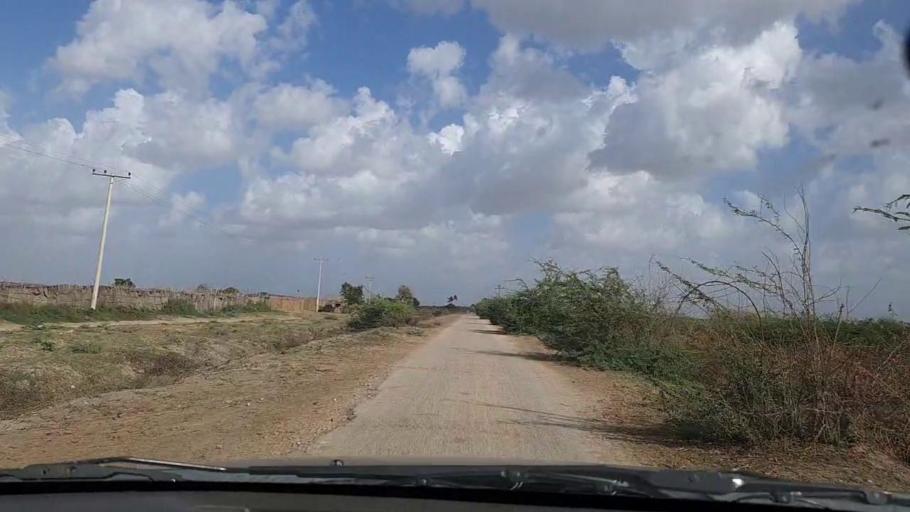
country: PK
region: Sindh
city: Keti Bandar
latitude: 24.0968
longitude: 67.6065
